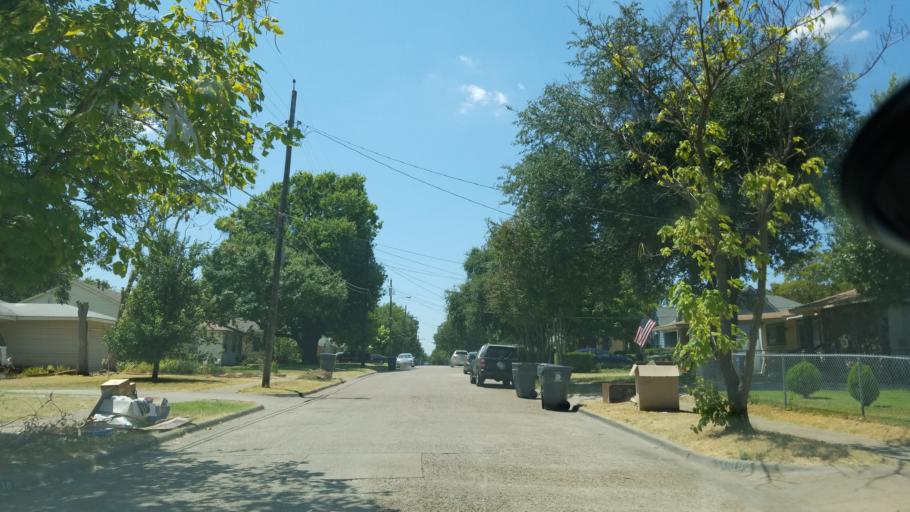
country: US
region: Texas
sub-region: Dallas County
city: Cockrell Hill
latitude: 32.7255
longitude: -96.8859
